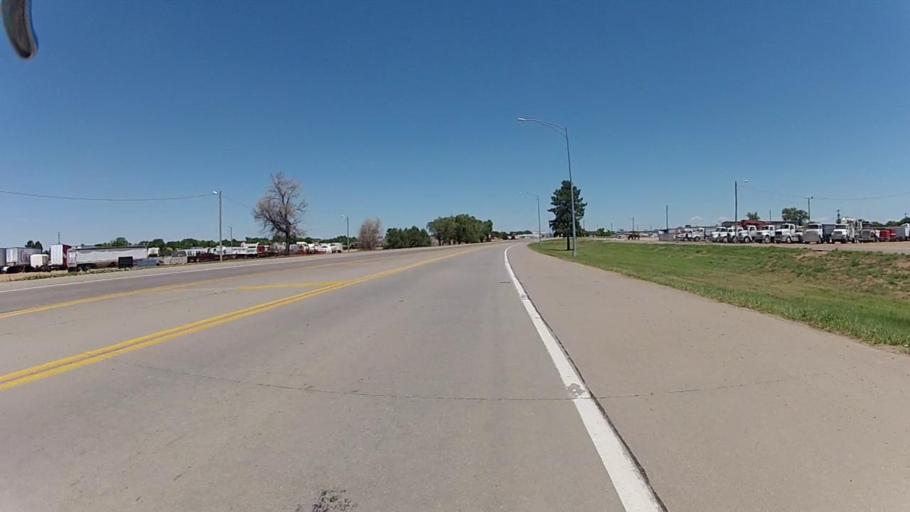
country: US
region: Kansas
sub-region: Ford County
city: Dodge City
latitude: 37.7297
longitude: -100.0186
